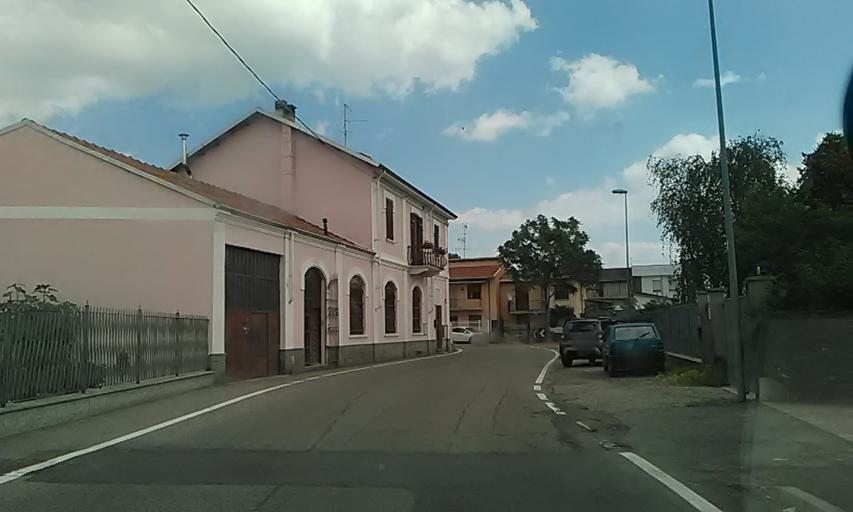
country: IT
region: Piedmont
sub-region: Provincia di Vercelli
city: Vercelli
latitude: 45.3040
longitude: 8.4444
